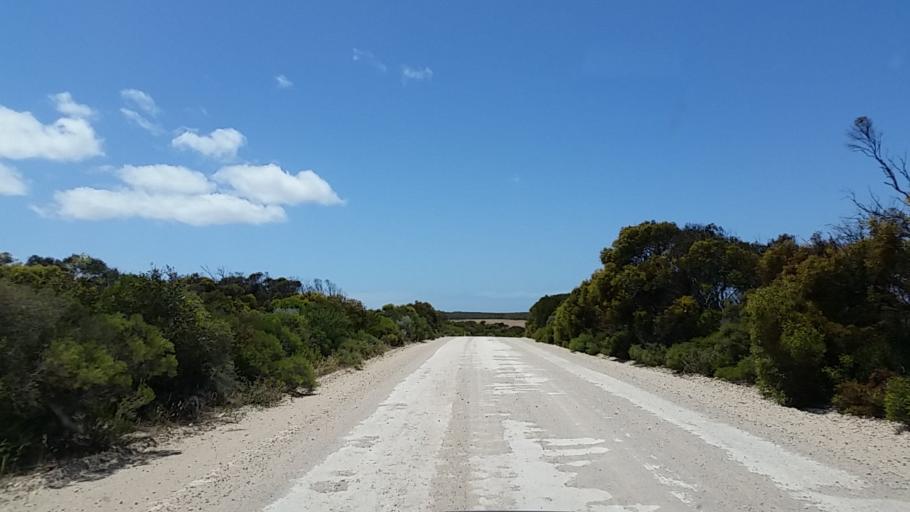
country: AU
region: South Australia
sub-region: Yorke Peninsula
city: Honiton
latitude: -35.2191
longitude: 137.0909
